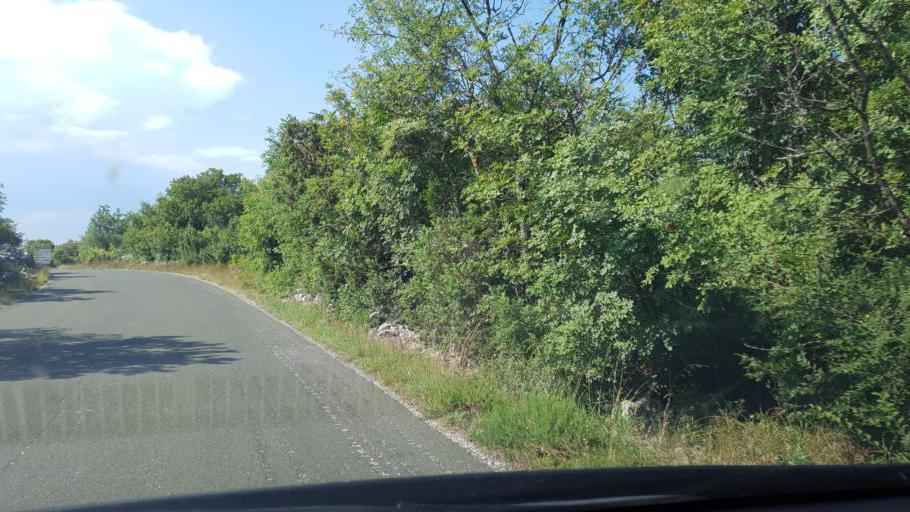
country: HR
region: Primorsko-Goranska
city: Omisalj
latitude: 45.1980
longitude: 14.5761
